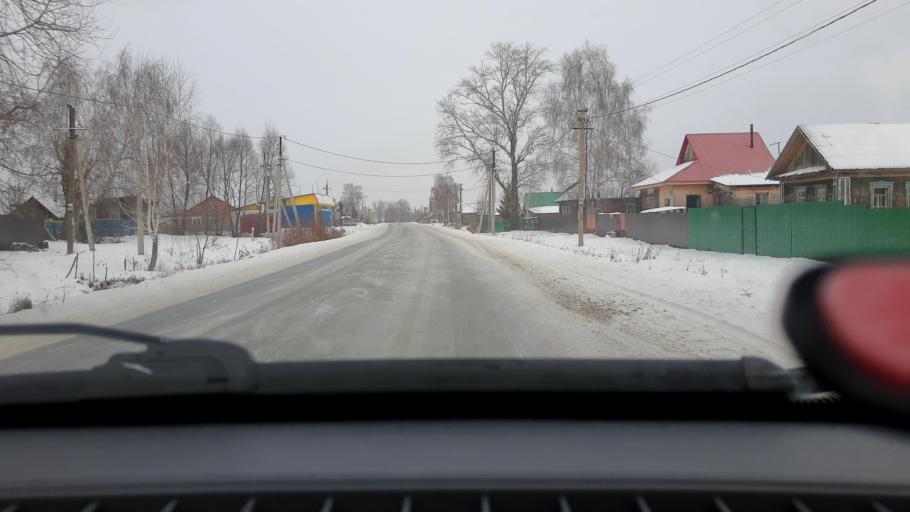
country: RU
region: Bashkortostan
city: Iglino
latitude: 54.7356
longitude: 56.3965
